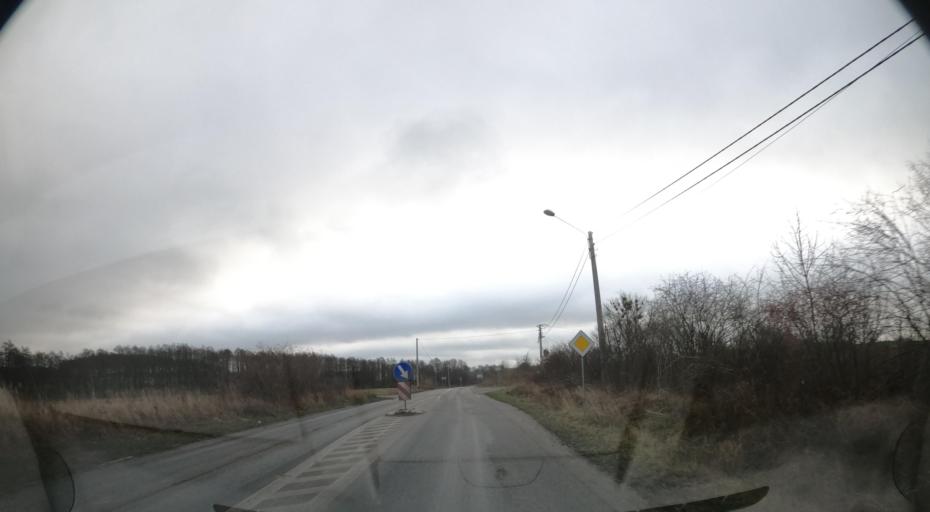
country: PL
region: Kujawsko-Pomorskie
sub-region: Powiat nakielski
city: Sadki
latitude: 53.1913
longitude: 17.3930
